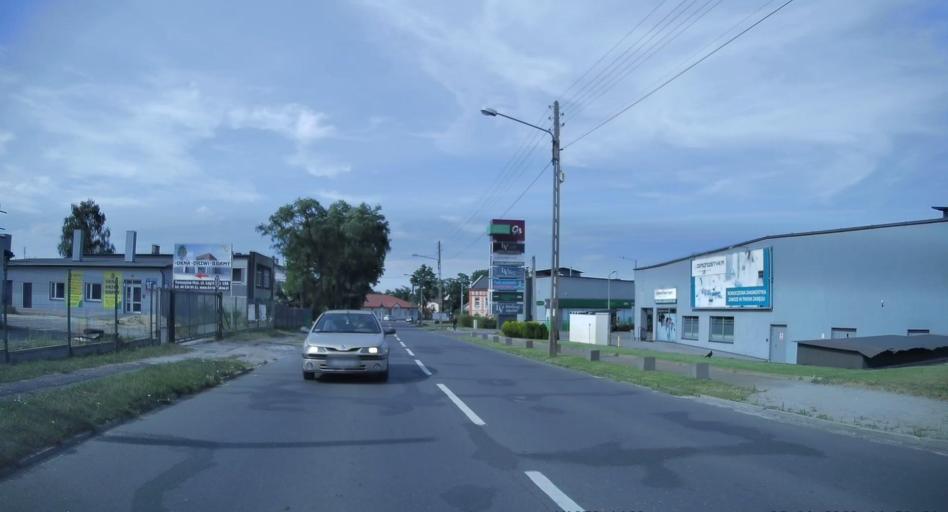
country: PL
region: Lodz Voivodeship
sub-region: Powiat tomaszowski
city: Tomaszow Mazowiecki
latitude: 51.5334
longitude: 19.9963
